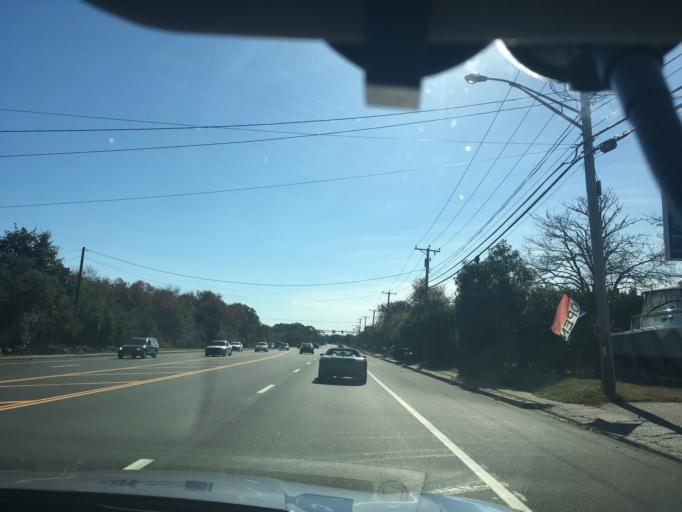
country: US
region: Rhode Island
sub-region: Washington County
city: Narragansett Pier
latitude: 41.3965
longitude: -71.4814
